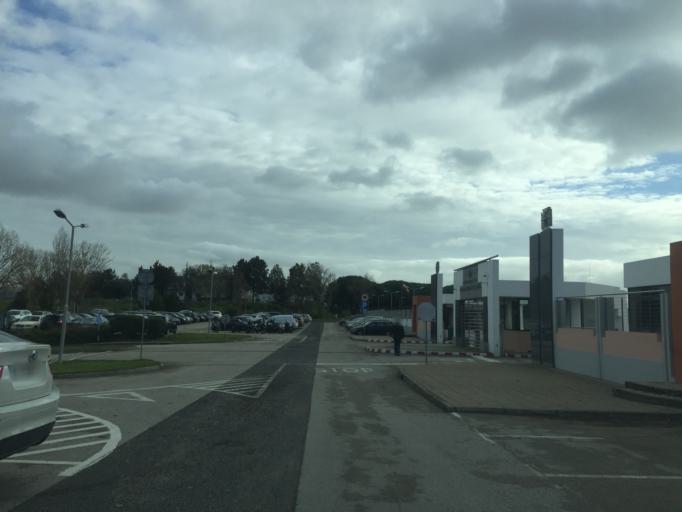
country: PT
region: Lisbon
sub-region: Amadora
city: Amadora
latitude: 38.7394
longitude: -9.2158
